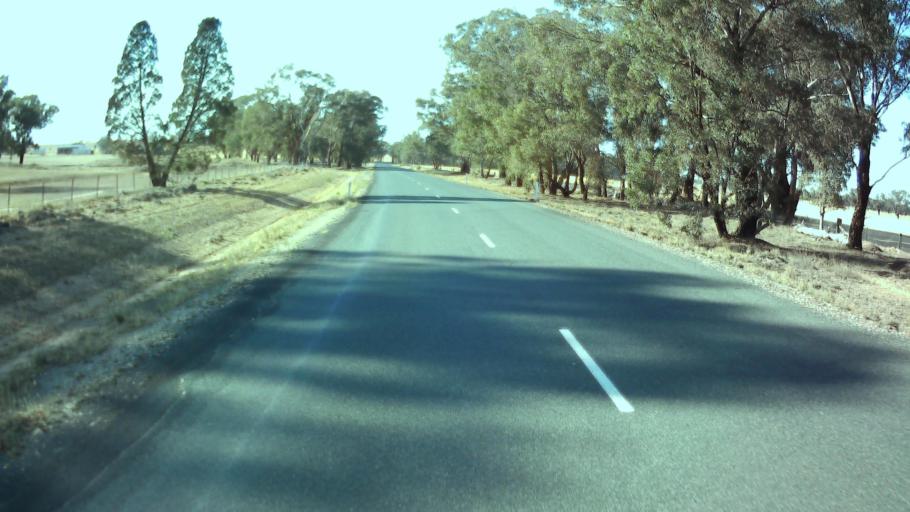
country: AU
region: New South Wales
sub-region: Weddin
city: Grenfell
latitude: -33.9454
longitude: 148.1358
